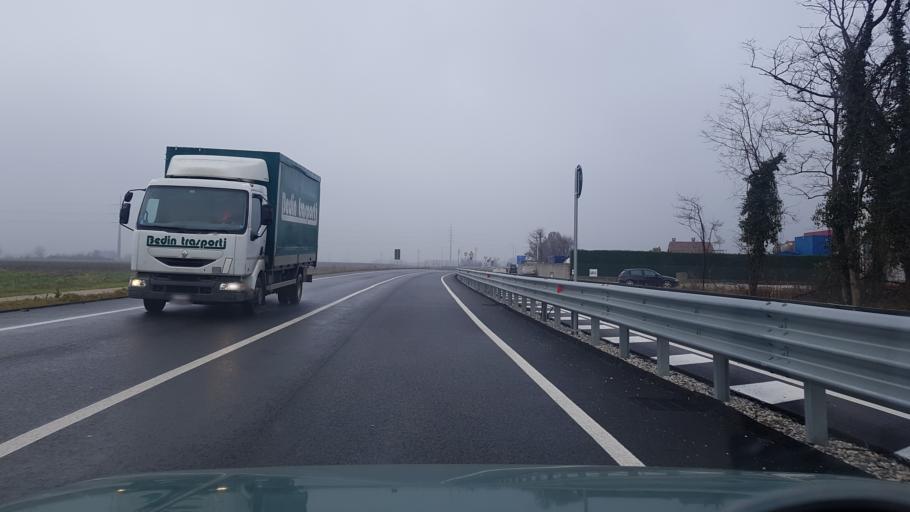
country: IT
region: Friuli Venezia Giulia
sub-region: Provincia di Udine
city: Ialmicco
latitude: 45.9197
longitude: 13.3686
